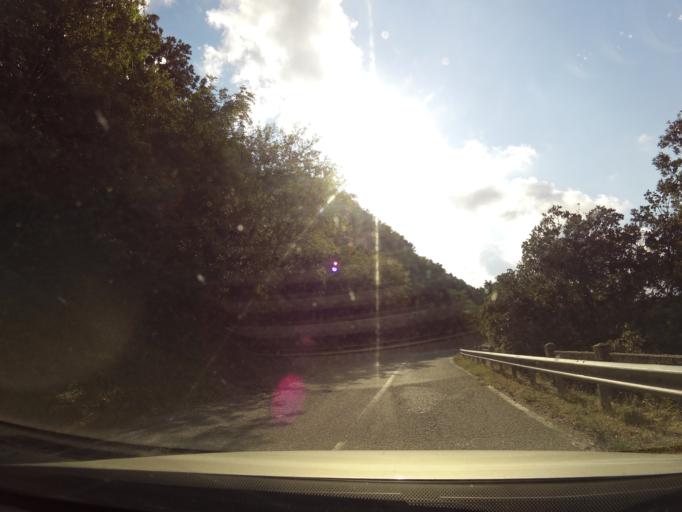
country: IT
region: Calabria
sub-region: Provincia di Reggio Calabria
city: Pazzano
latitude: 38.4678
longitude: 16.4242
